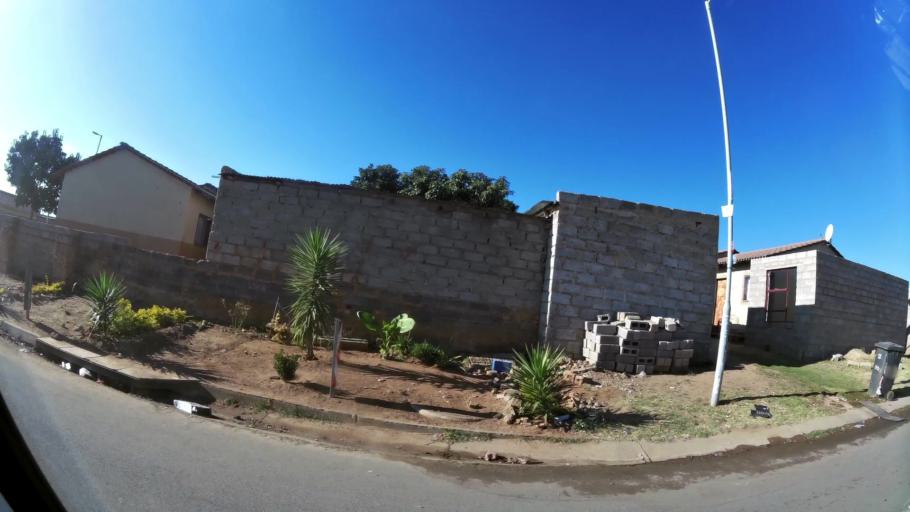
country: ZA
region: Gauteng
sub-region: City of Johannesburg Metropolitan Municipality
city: Diepsloot
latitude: -25.8992
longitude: 28.0970
